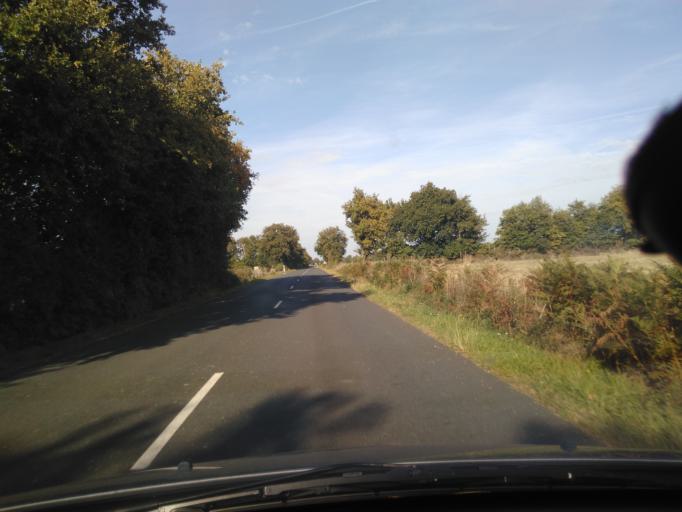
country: FR
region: Pays de la Loire
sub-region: Departement de la Vendee
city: Grosbreuil
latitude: 46.5172
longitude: -1.5592
